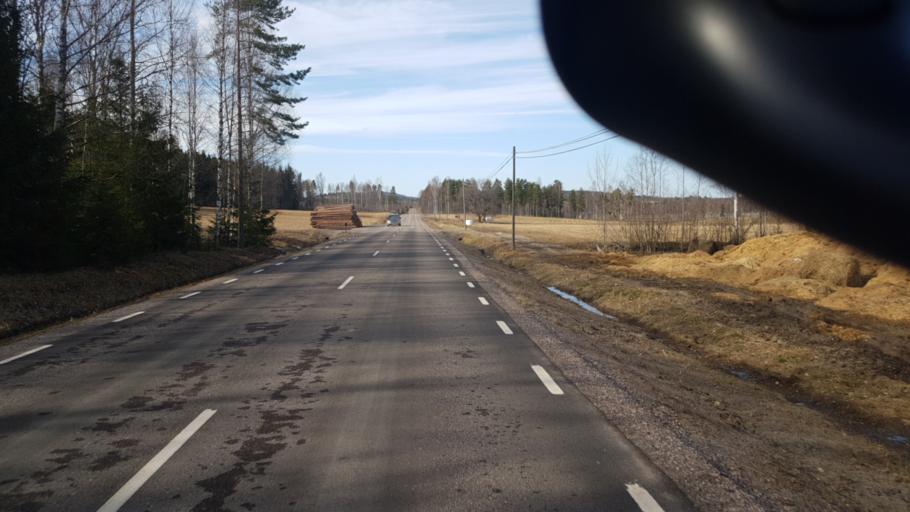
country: SE
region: Vaermland
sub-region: Eda Kommun
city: Amotfors
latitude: 59.7439
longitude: 12.3765
